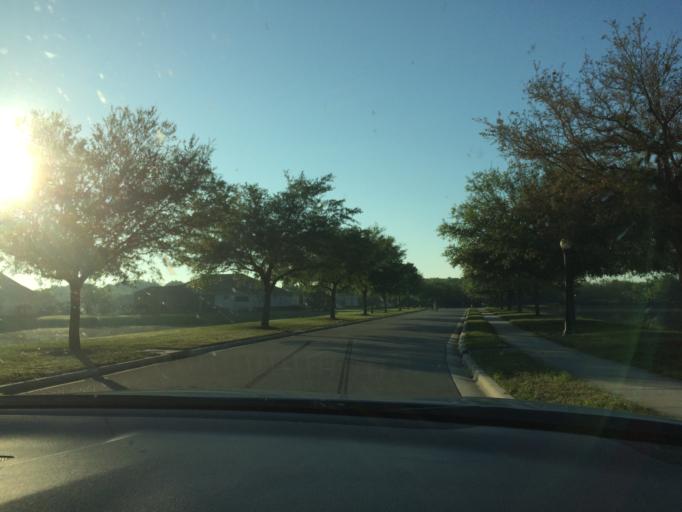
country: US
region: Florida
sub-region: Manatee County
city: Ellenton
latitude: 27.4957
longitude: -82.4130
